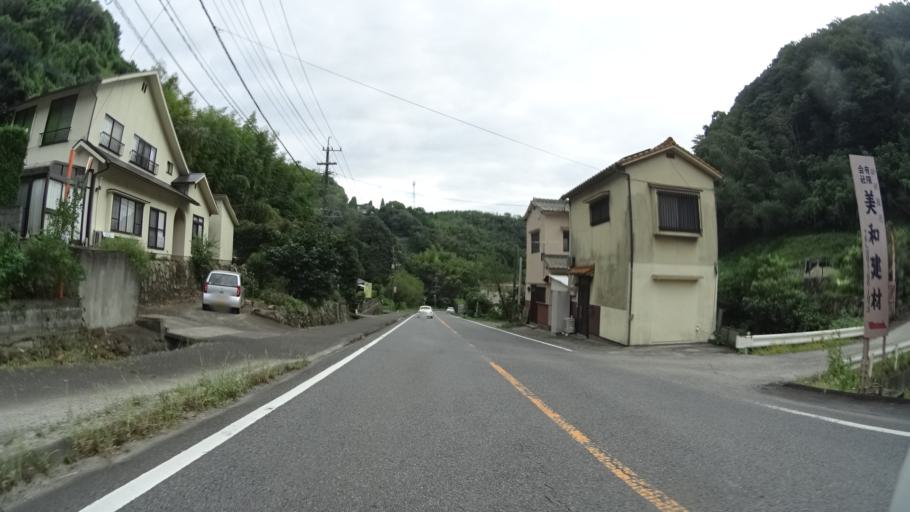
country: JP
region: Oita
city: Beppu
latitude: 33.3272
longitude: 131.4753
